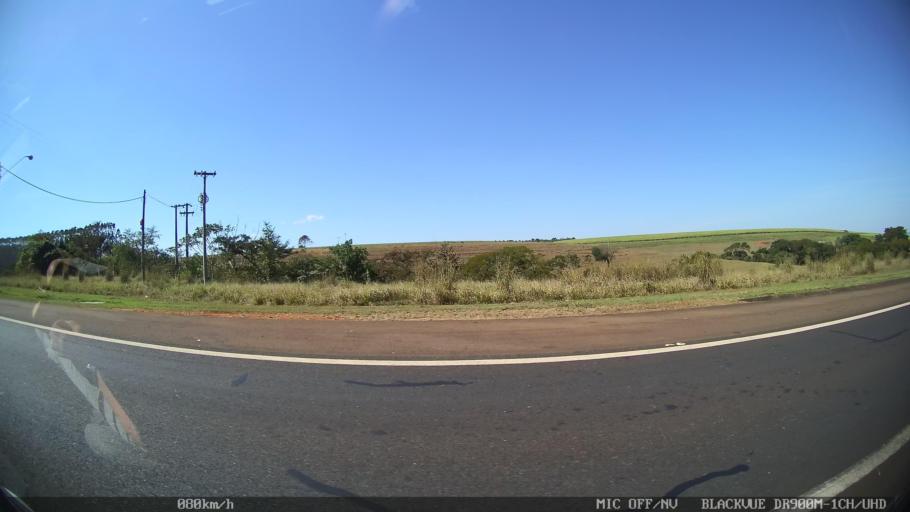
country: BR
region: Sao Paulo
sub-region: Franca
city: Franca
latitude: -20.6970
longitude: -47.4998
